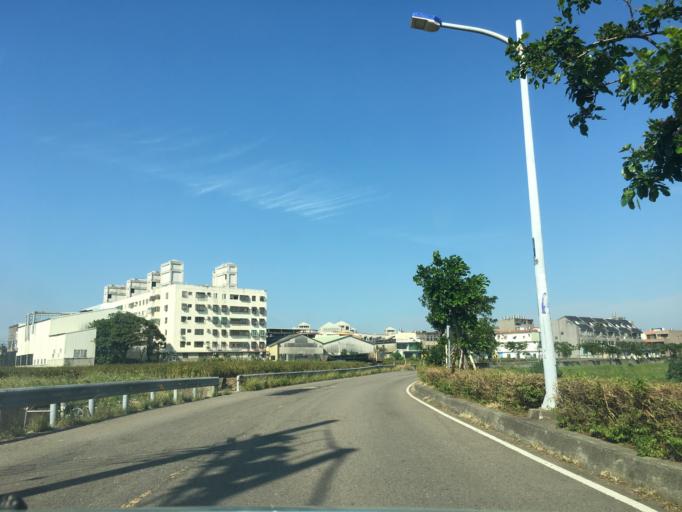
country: TW
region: Taiwan
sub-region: Hsinchu
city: Hsinchu
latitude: 24.8029
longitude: 120.9413
